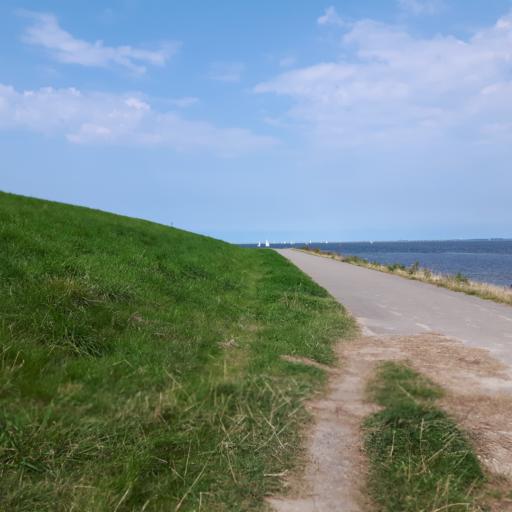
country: NL
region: Zeeland
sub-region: Gemeente Goes
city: Goes
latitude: 51.5413
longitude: 3.9284
